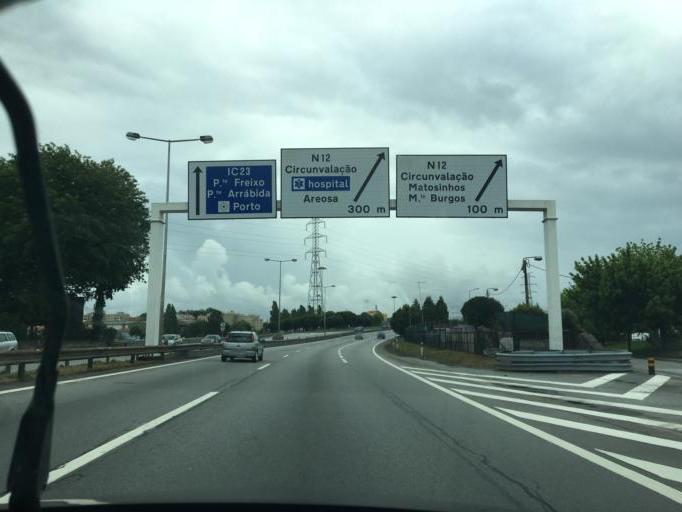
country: PT
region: Porto
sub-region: Matosinhos
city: Sao Mamede de Infesta
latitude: 41.1838
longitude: -8.6231
